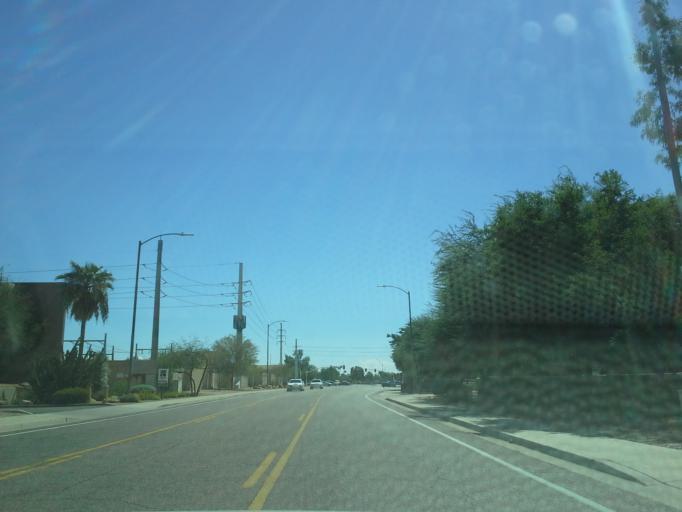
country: US
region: Arizona
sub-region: Maricopa County
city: Scottsdale
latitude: 33.5848
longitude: -111.8861
